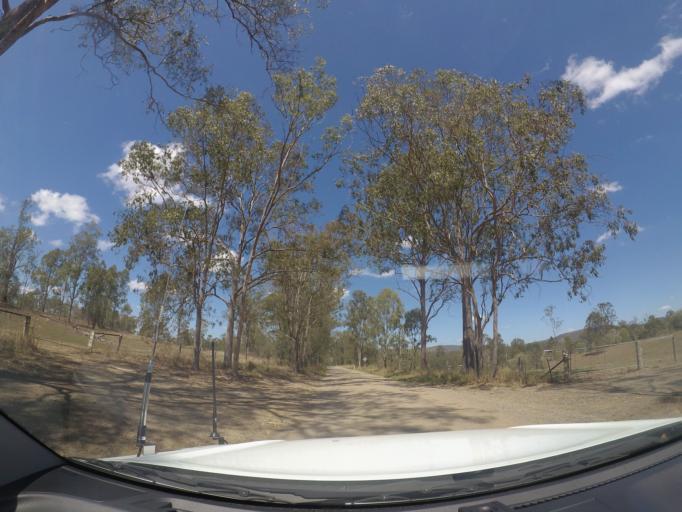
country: AU
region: Queensland
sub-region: Logan
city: Cedar Vale
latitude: -27.8475
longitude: 152.8968
